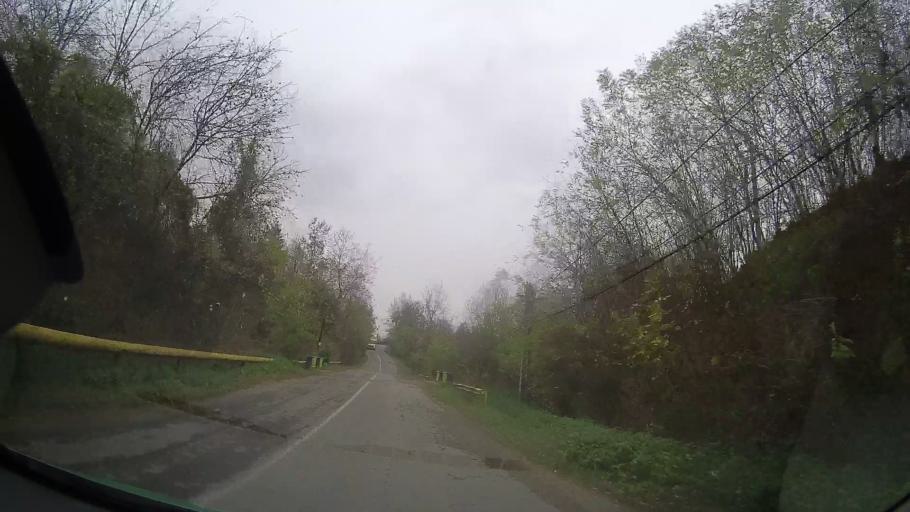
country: RO
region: Prahova
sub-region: Comuna Ceptura
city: Ceptura de Jos
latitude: 45.0325
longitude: 26.3196
